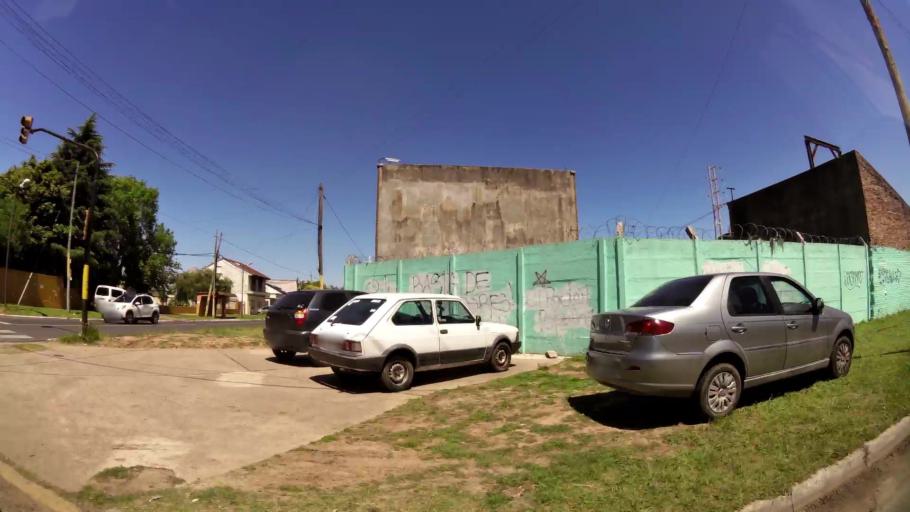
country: AR
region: Buenos Aires
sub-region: Partido de Quilmes
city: Quilmes
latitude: -34.7242
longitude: -58.2809
